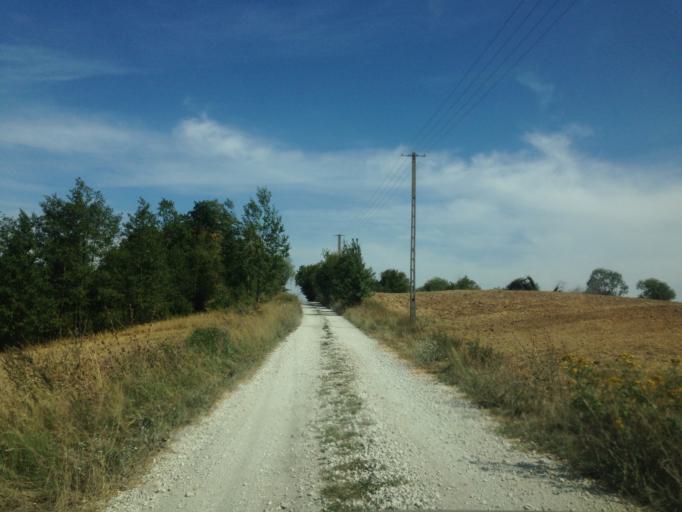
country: PL
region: Kujawsko-Pomorskie
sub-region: Powiat brodnicki
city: Bartniczka
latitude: 53.2348
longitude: 19.5718
